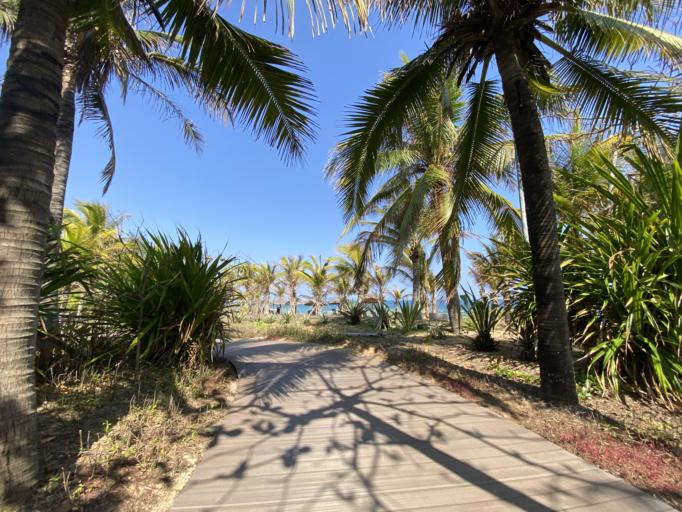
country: CN
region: Hainan
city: Haitangwan
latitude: 18.3483
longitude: 109.7399
